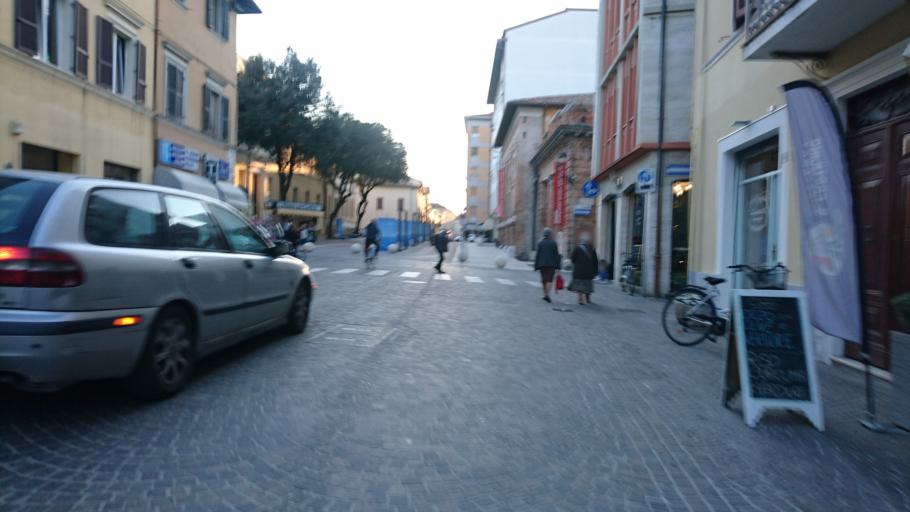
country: IT
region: The Marches
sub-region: Provincia di Pesaro e Urbino
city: Pesaro
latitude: 43.9120
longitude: 12.9088
